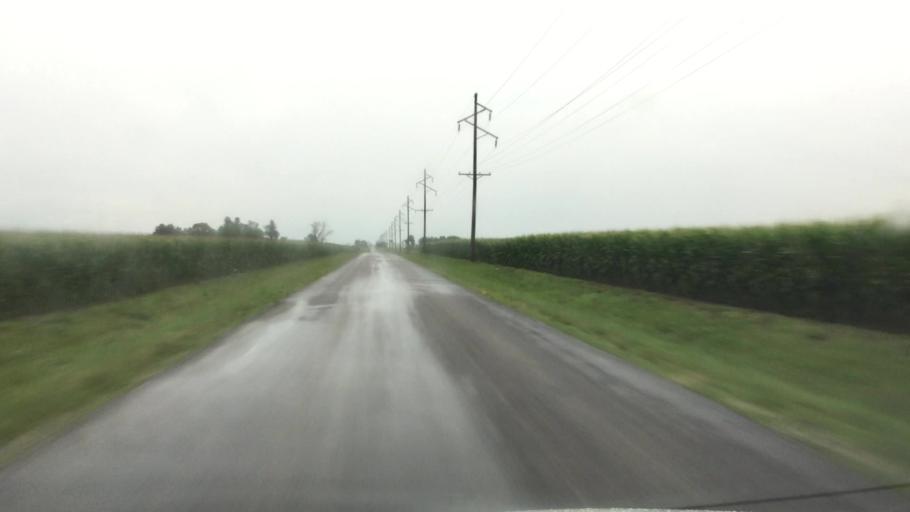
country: US
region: Illinois
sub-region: Hancock County
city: Nauvoo
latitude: 40.5116
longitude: -91.2694
